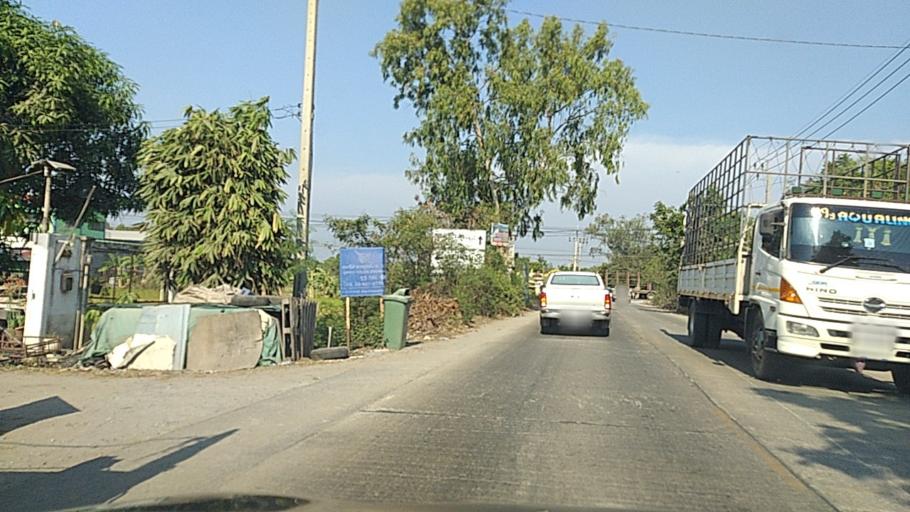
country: TH
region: Nonthaburi
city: Bang Yai
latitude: 13.8821
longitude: 100.3263
